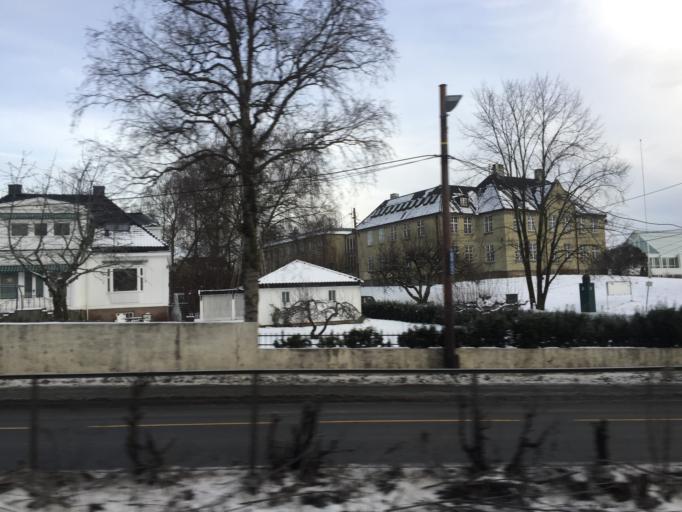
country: NO
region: Oslo
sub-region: Oslo
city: Sjolyststranda
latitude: 59.9373
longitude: 10.7066
